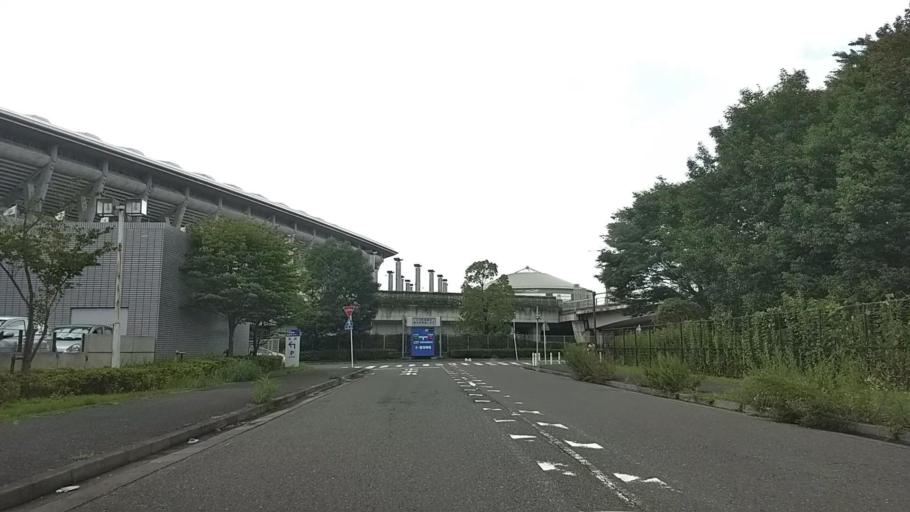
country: JP
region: Kanagawa
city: Yokohama
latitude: 35.5103
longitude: 139.6090
